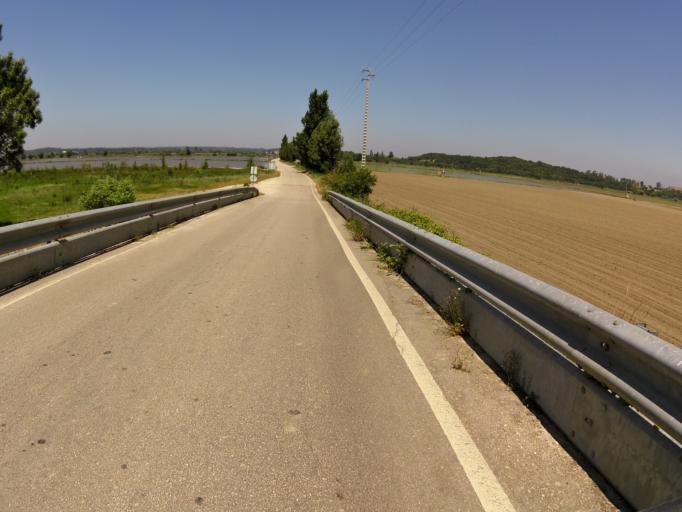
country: PT
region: Coimbra
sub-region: Montemor-O-Velho
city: Montemor-o-Velho
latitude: 40.1604
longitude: -8.7147
